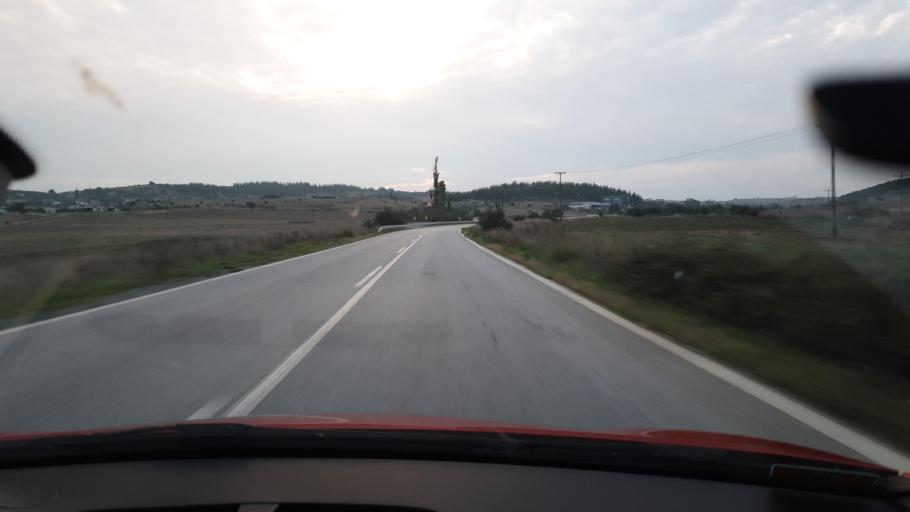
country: GR
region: Central Macedonia
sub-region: Nomos Kilkis
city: Kristoni
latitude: 40.9952
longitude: 22.7442
